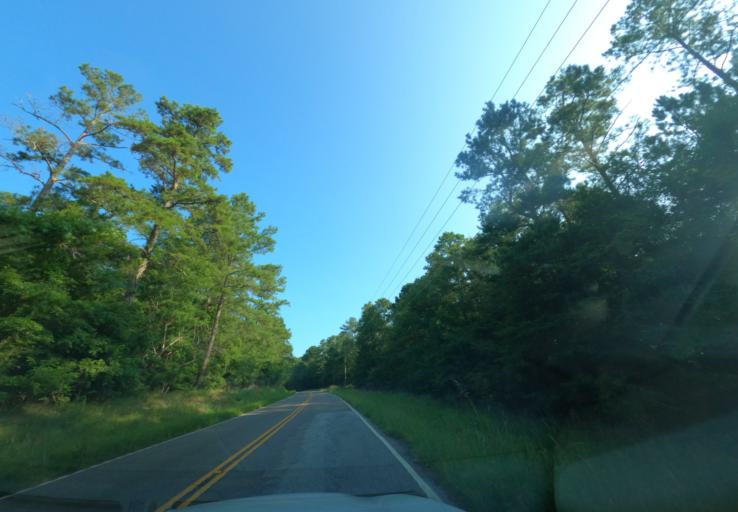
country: US
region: South Carolina
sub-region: Edgefield County
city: Murphys Estates
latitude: 33.6743
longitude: -81.9790
